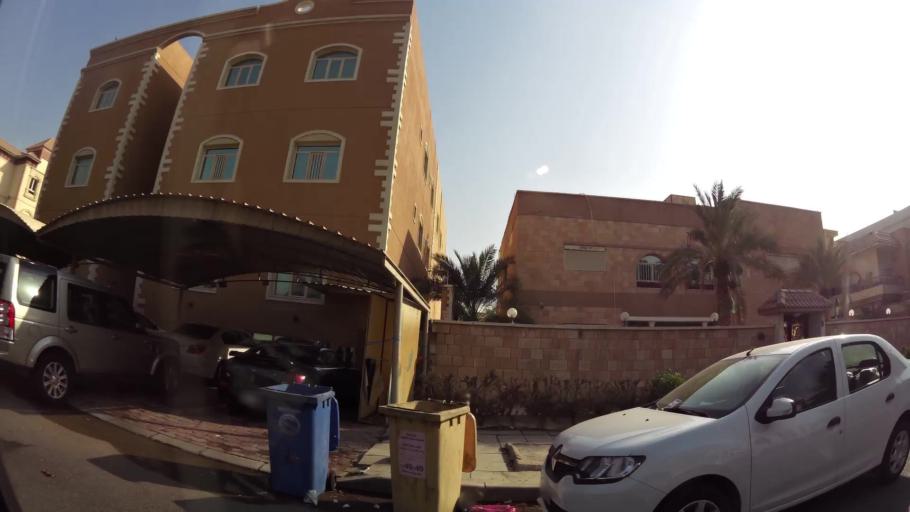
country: KW
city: Bayan
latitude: 29.3147
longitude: 48.0455
